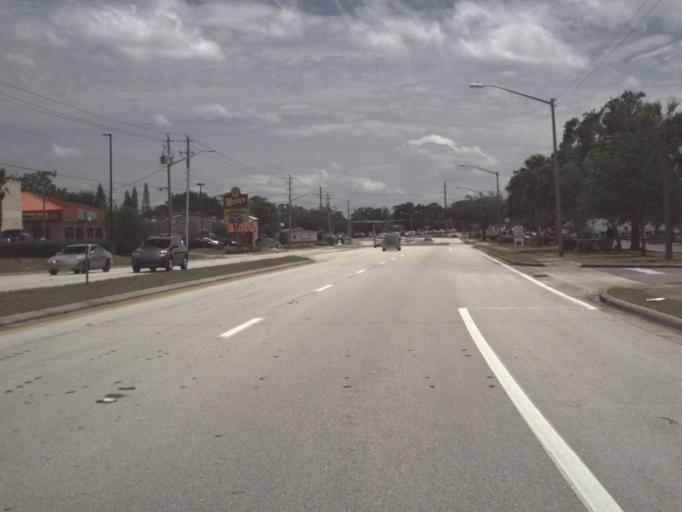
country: US
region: Florida
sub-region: Brevard County
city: Titusville
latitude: 28.6181
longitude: -80.8422
